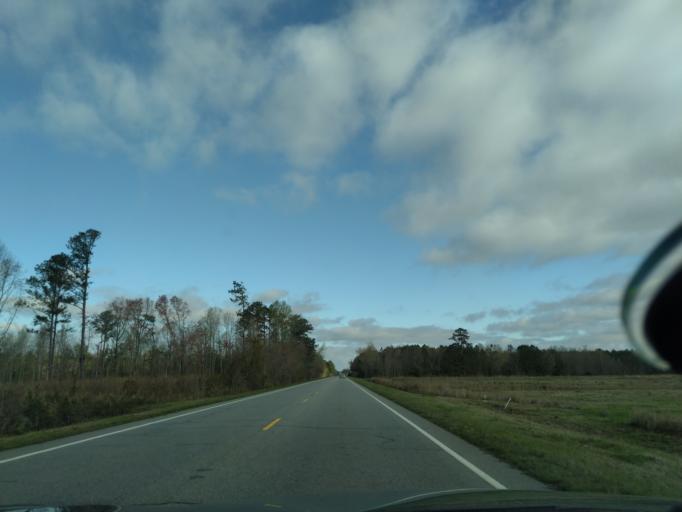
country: US
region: North Carolina
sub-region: Washington County
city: Plymouth
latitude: 35.9972
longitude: -76.7717
